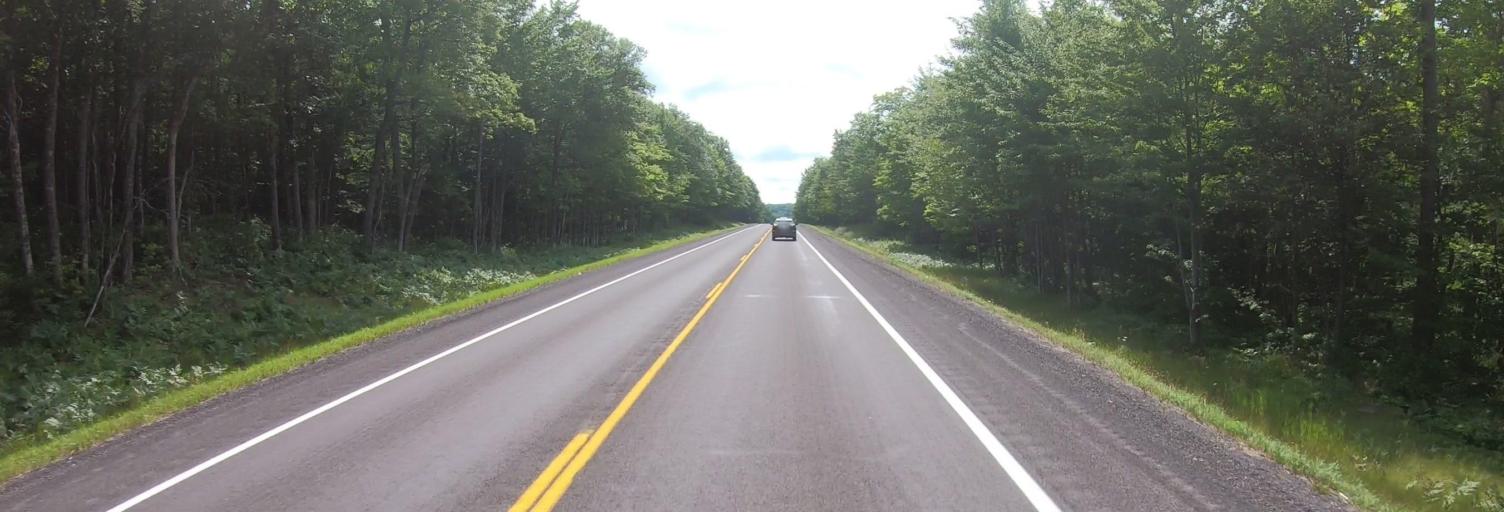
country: US
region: Michigan
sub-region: Houghton County
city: Hancock
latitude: 47.0312
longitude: -88.6916
